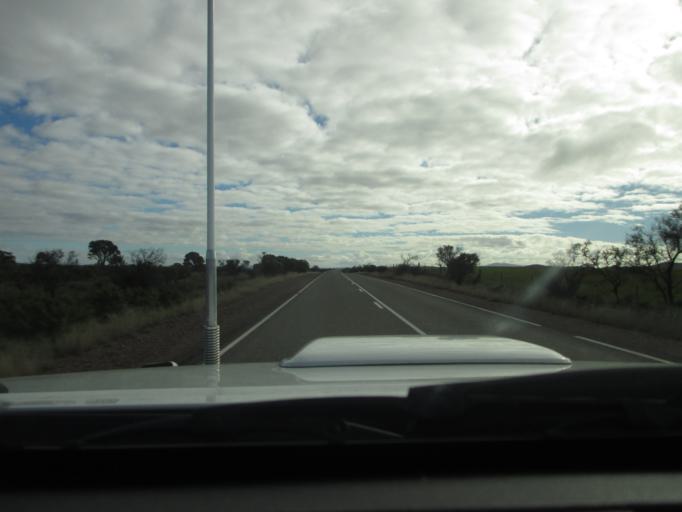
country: AU
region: South Australia
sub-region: Flinders Ranges
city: Quorn
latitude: -32.4573
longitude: 138.5376
